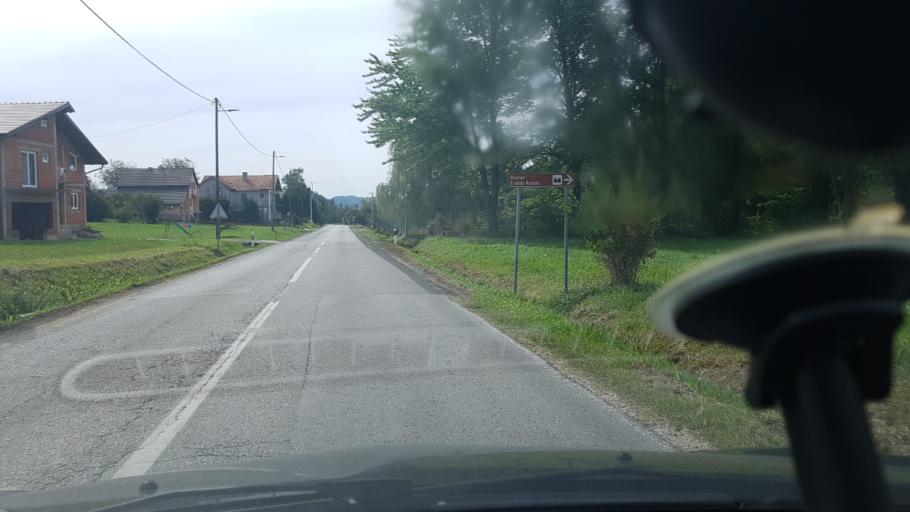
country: HR
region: Varazdinska
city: Ljubescica
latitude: 46.1063
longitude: 16.3935
